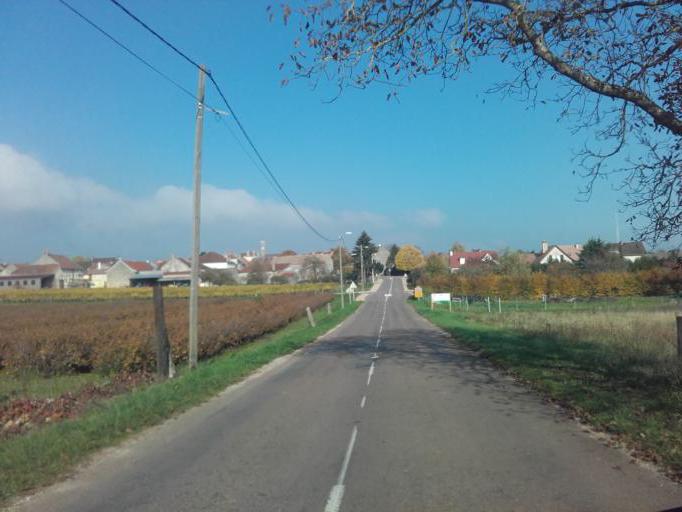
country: FR
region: Bourgogne
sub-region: Departement de la Cote-d'Or
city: Nuits-Saint-Georges
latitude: 47.1261
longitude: 4.9042
